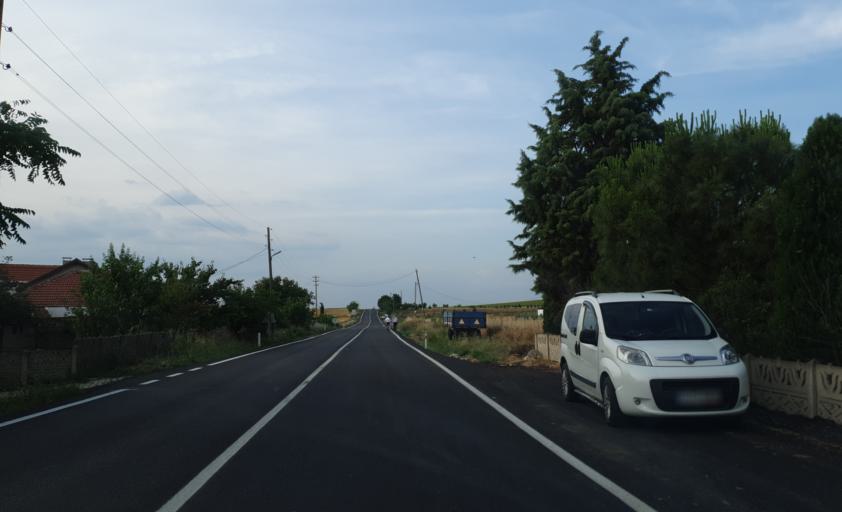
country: TR
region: Tekirdag
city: Hayrabolu
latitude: 41.2930
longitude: 27.1346
